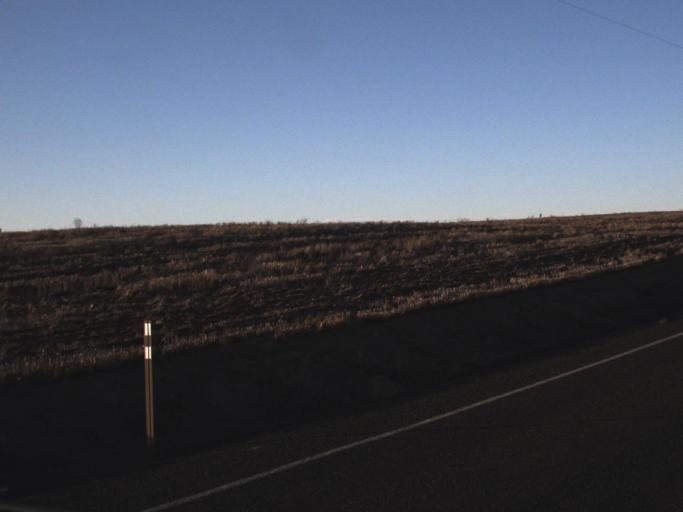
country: US
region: Washington
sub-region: Franklin County
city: Connell
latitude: 46.7526
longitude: -118.5476
